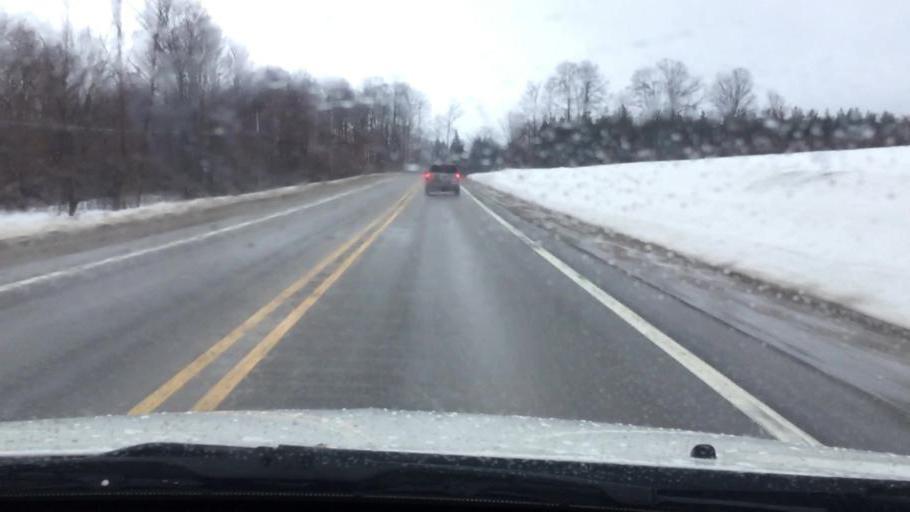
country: US
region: Michigan
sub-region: Charlevoix County
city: East Jordan
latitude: 45.1953
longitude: -85.1647
